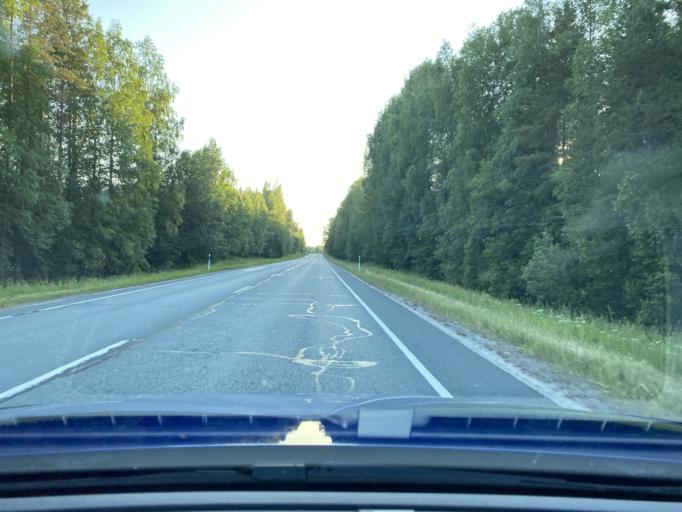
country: FI
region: Haeme
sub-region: Forssa
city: Tammela
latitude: 60.8265
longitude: 23.9412
